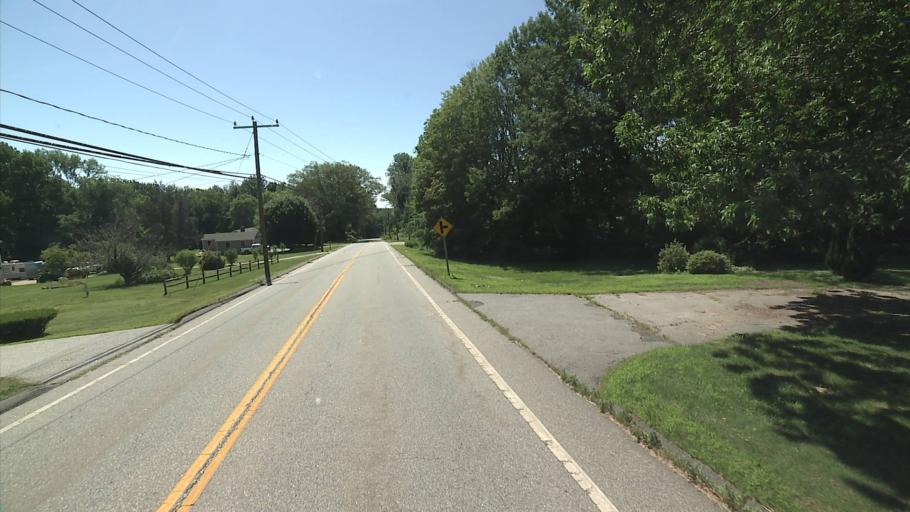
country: US
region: Connecticut
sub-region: Windham County
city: Willimantic
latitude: 41.6749
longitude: -72.2303
